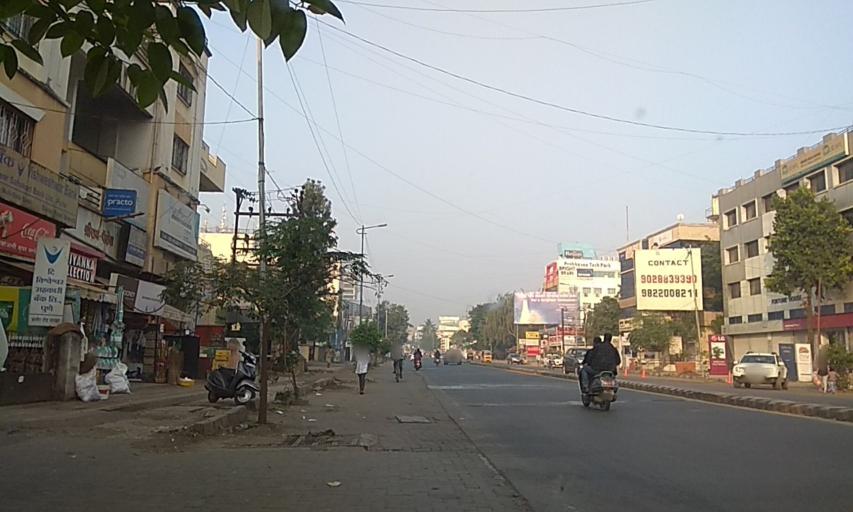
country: IN
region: Maharashtra
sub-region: Pune Division
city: Pimpri
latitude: 18.5641
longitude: 73.7805
